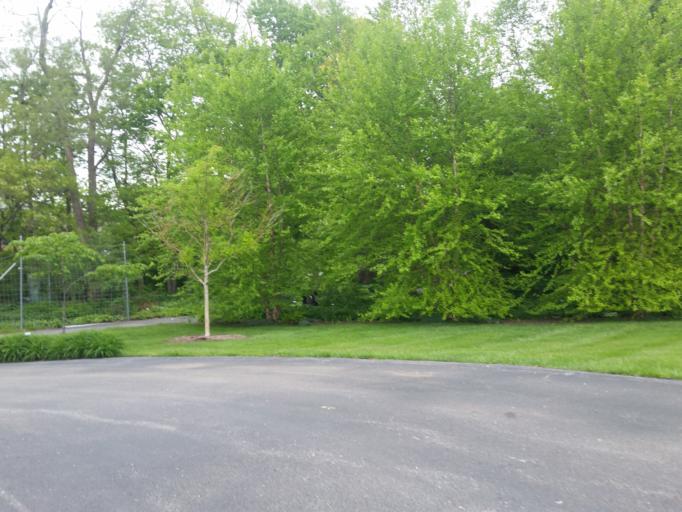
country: US
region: Nebraska
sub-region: Douglas County
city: Omaha
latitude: 41.2402
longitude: -95.9224
